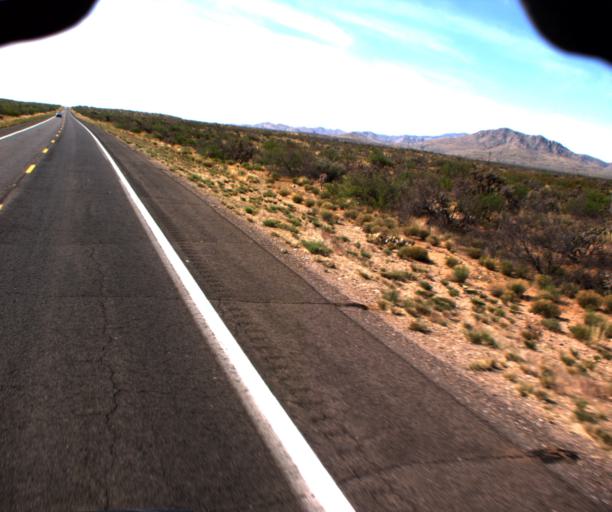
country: US
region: Arizona
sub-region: Graham County
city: Swift Trail Junction
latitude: 32.6449
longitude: -109.6965
